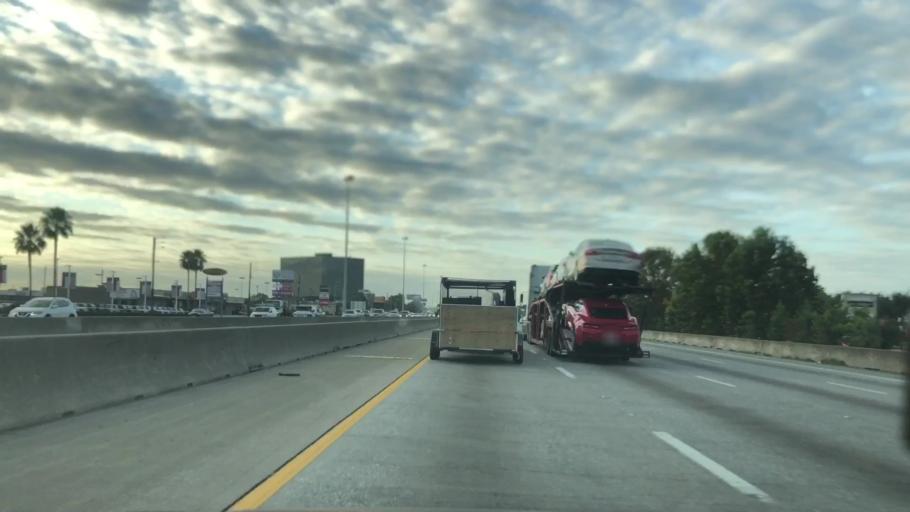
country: US
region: Texas
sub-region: Harris County
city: Aldine
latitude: 29.9262
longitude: -95.4122
